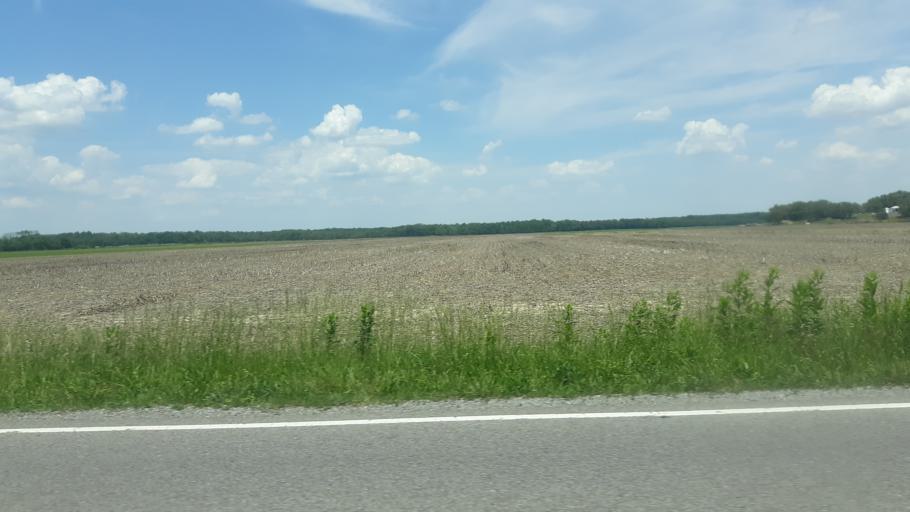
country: US
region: Illinois
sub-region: Saline County
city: Harrisburg
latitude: 37.6365
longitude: -88.5124
